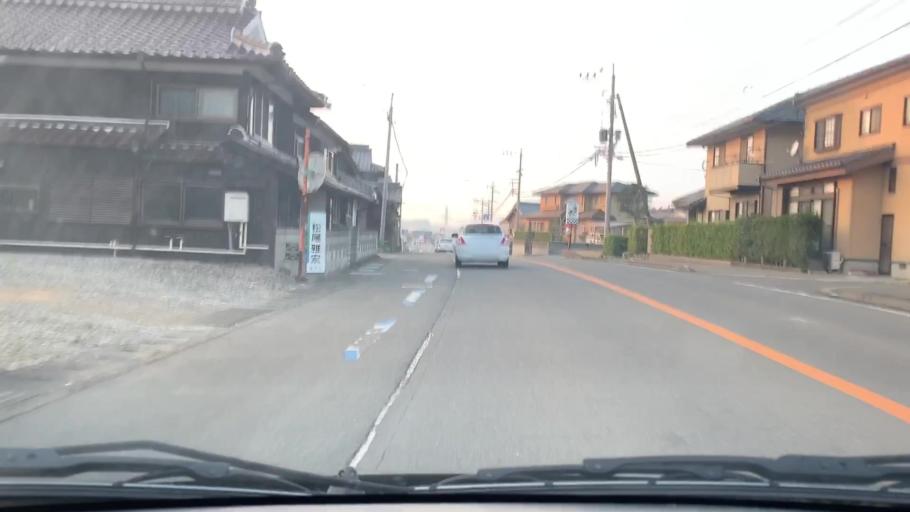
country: JP
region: Saga Prefecture
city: Imaricho-ko
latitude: 33.2673
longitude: 129.9004
